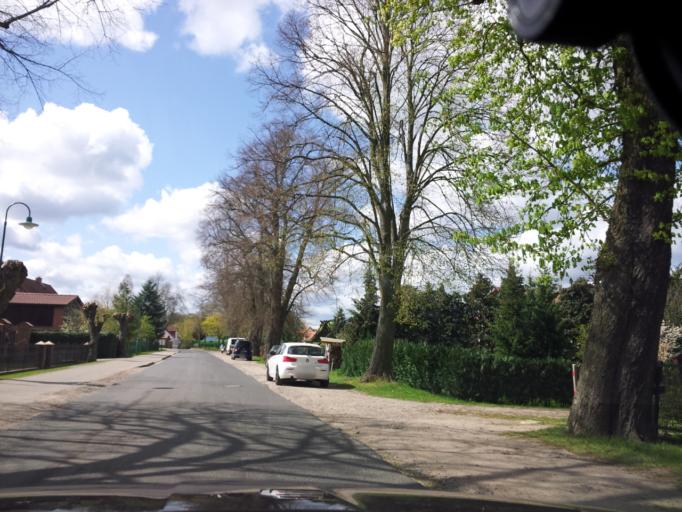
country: DE
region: Brandenburg
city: Rudnitz
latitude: 52.7220
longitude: 13.6223
